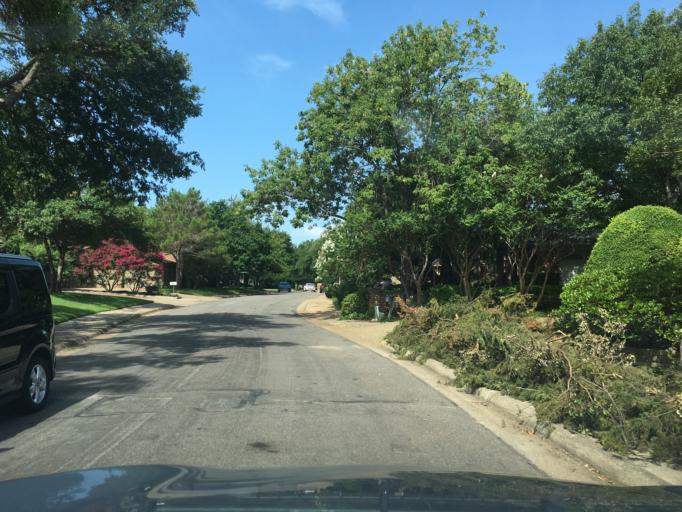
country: US
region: Texas
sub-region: Dallas County
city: Addison
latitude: 32.9285
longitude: -96.7936
